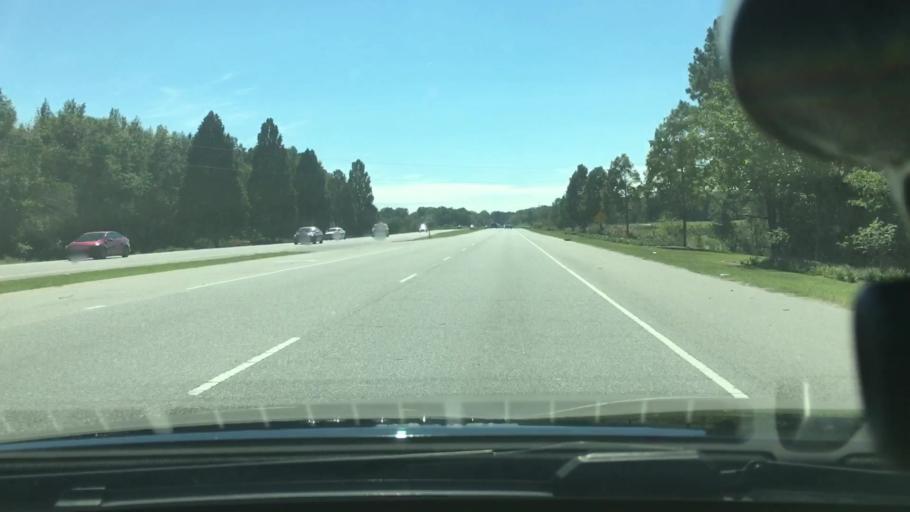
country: US
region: North Carolina
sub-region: Pitt County
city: Greenville
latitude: 35.6273
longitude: -77.3821
